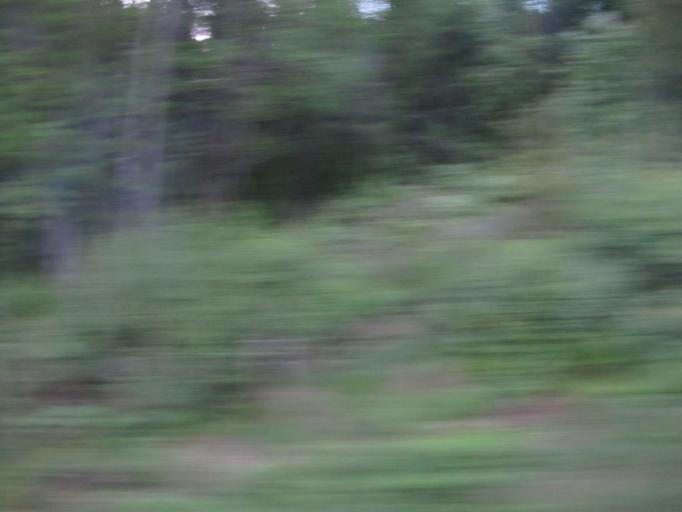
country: NO
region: Oppland
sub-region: Lillehammer
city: Lillehammer
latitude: 61.0508
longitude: 10.4595
